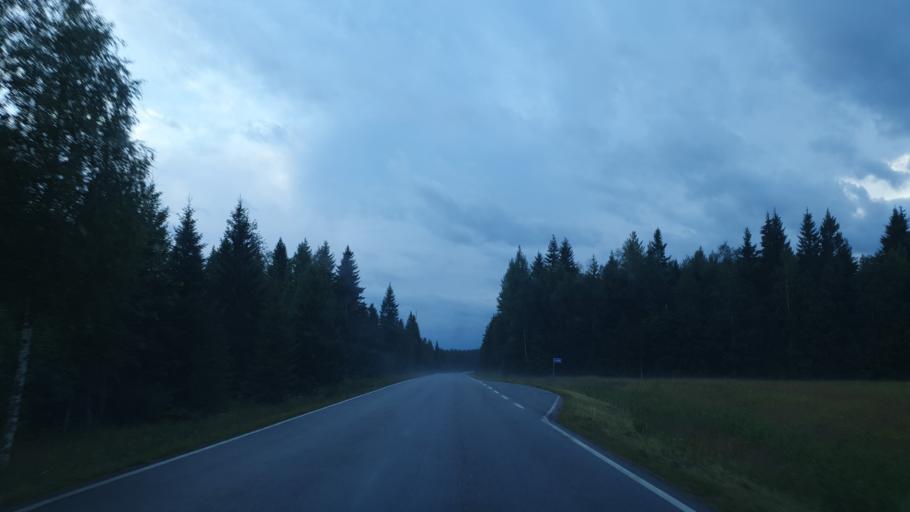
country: FI
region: Kainuu
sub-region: Kehys-Kainuu
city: Kuhmo
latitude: 63.9561
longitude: 29.7116
